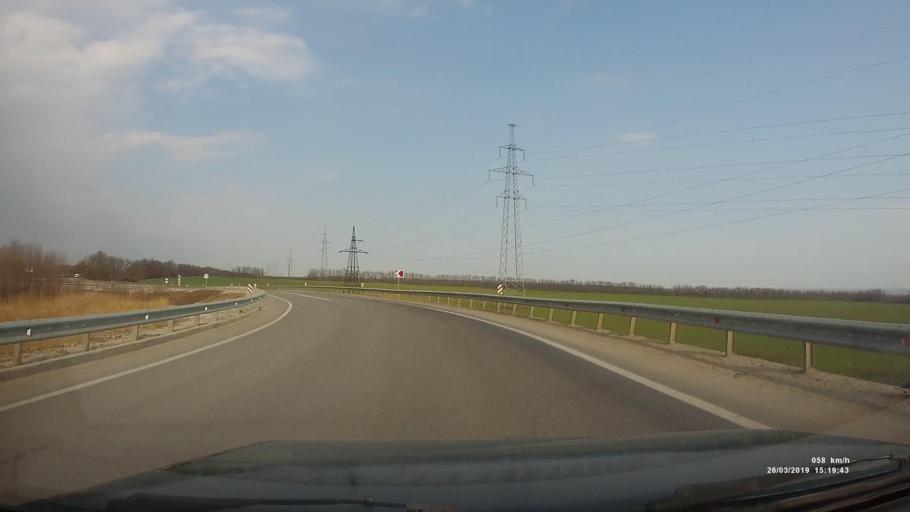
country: RU
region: Rostov
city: Taganrog
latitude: 47.2850
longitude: 38.9592
